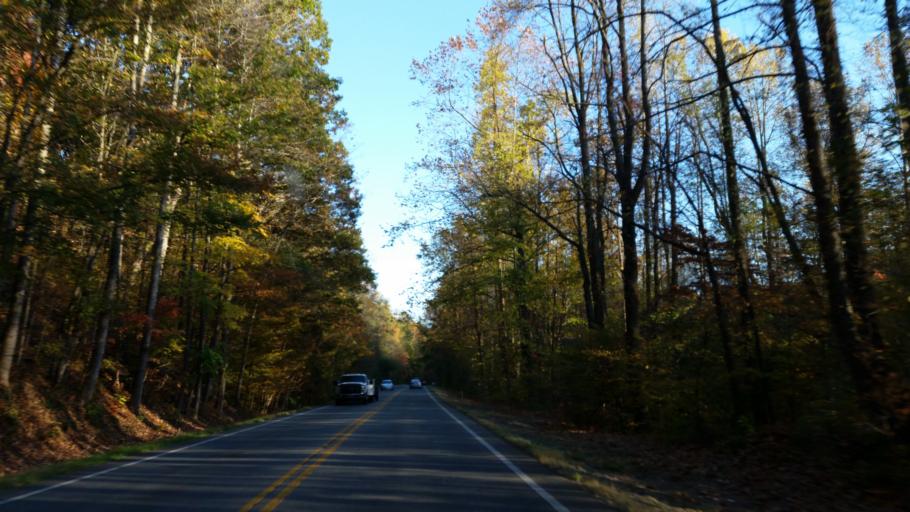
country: US
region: Georgia
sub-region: Pickens County
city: Jasper
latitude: 34.5615
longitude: -84.3014
